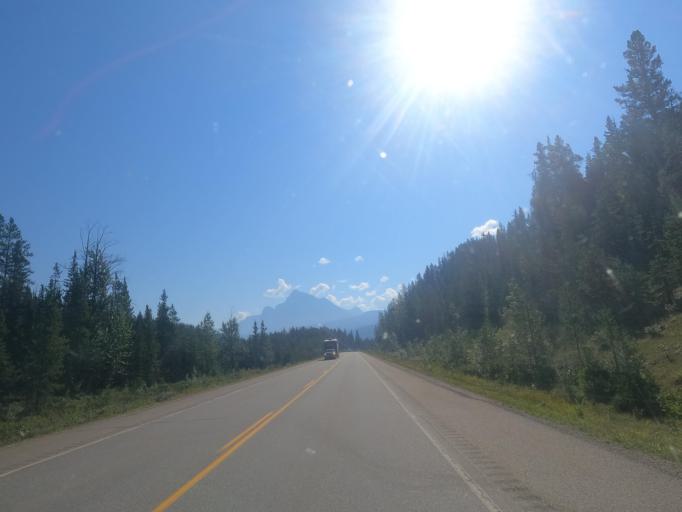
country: CA
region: Alberta
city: Jasper Park Lodge
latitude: 52.8579
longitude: -118.6314
